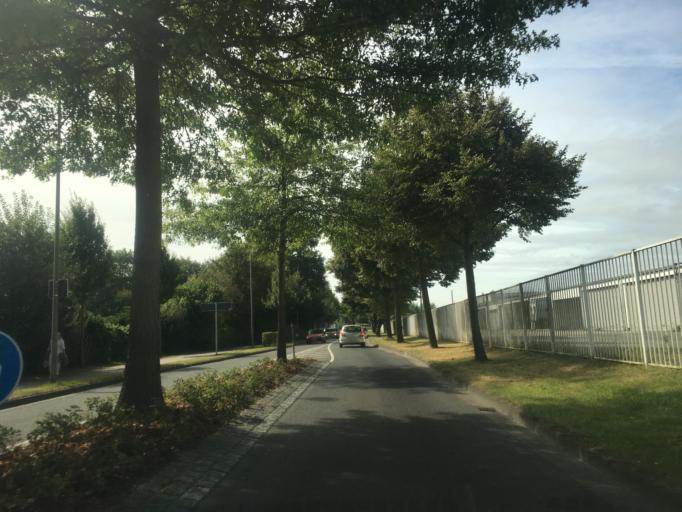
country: DE
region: North Rhine-Westphalia
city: Erkelenz
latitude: 51.0725
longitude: 6.3053
